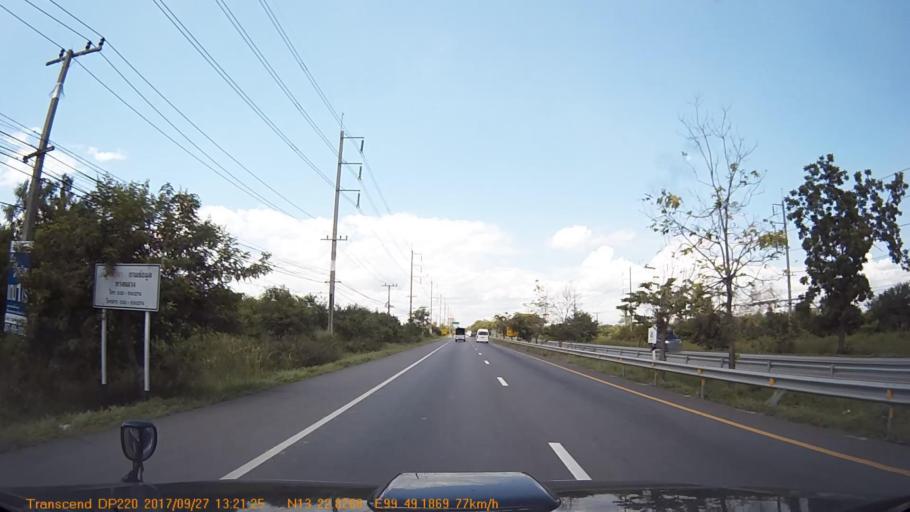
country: TH
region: Ratchaburi
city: Pak Tho
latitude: 13.3805
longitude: 99.8198
